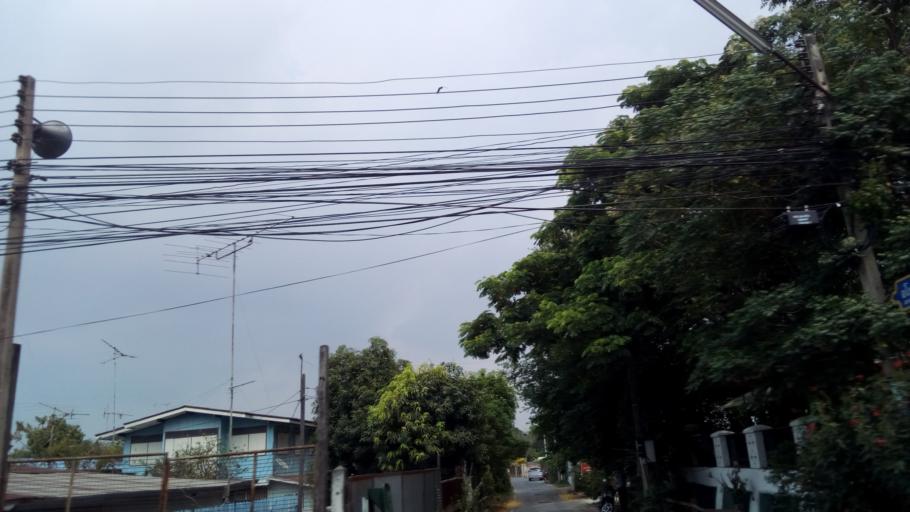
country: TH
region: Phra Nakhon Si Ayutthaya
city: Phra Nakhon Si Ayutthaya
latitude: 14.3488
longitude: 100.5919
